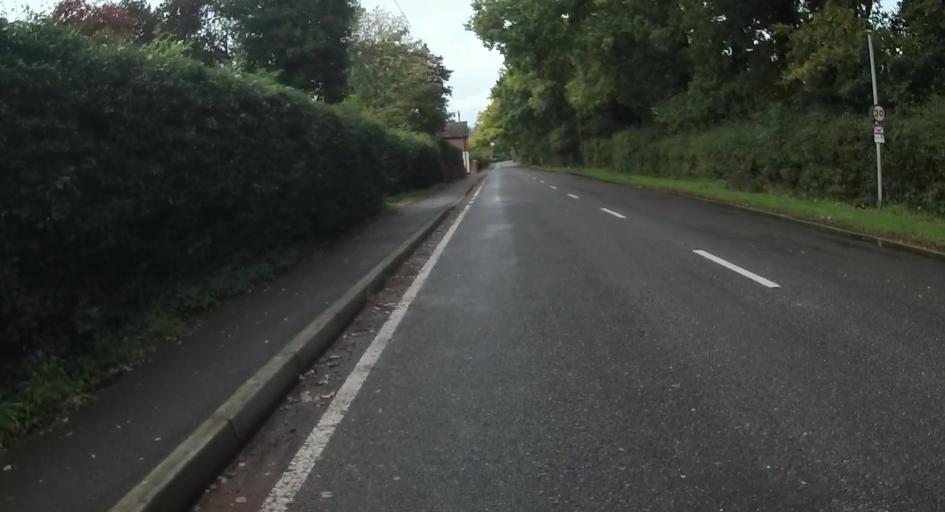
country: GB
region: England
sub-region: Hampshire
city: Tadley
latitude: 51.3501
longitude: -1.1664
